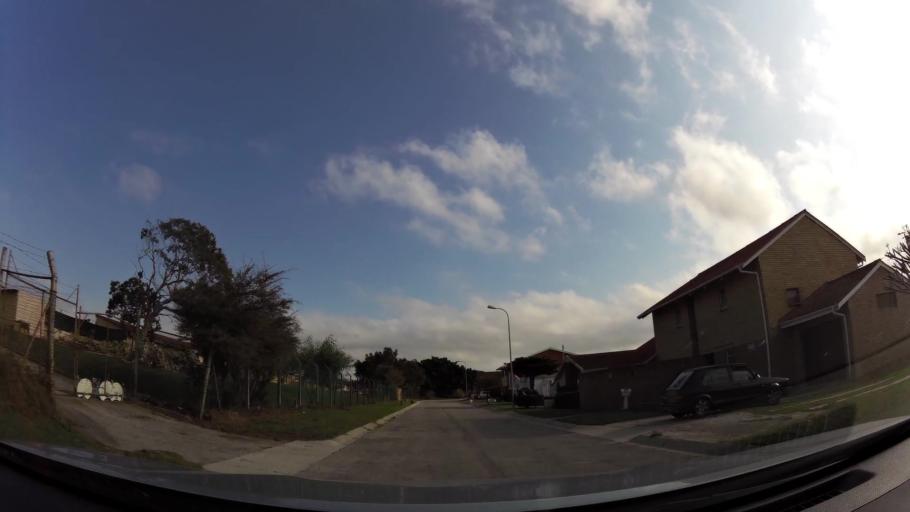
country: ZA
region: Eastern Cape
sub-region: Nelson Mandela Bay Metropolitan Municipality
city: Port Elizabeth
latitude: -33.9239
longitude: 25.5606
